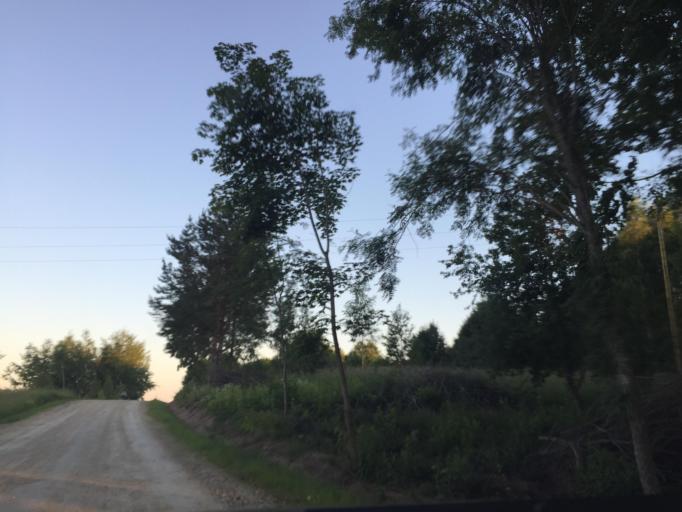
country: LV
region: Rezekne
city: Rezekne
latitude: 56.3633
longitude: 27.4118
